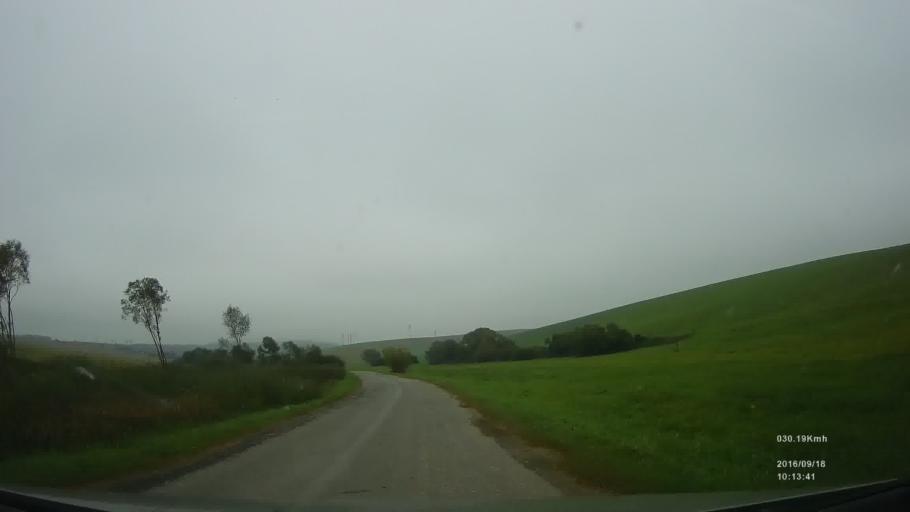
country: SK
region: Kosicky
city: Spisska Nova Ves
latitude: 48.9362
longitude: 20.6314
